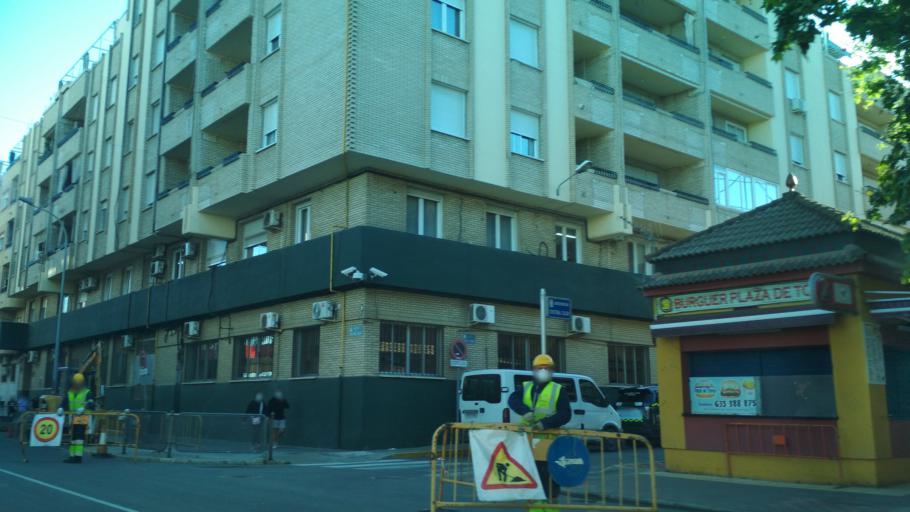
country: ES
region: Andalusia
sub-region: Provincia de Huelva
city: Huelva
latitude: 37.2659
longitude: -6.9522
